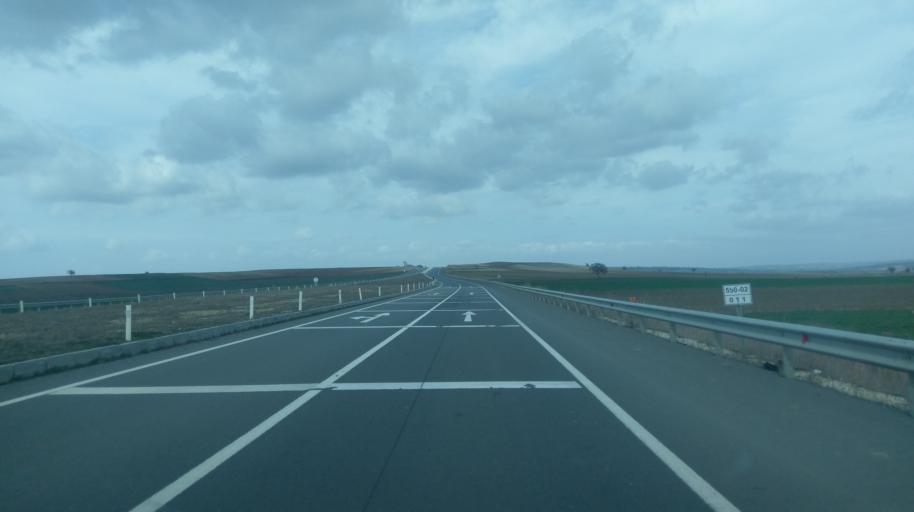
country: TR
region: Edirne
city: Ibriktepe
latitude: 41.0096
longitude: 26.6372
